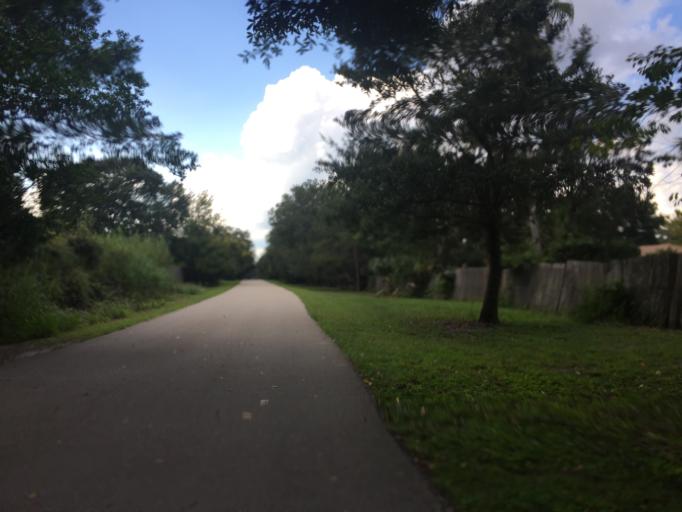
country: US
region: Florida
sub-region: Seminole County
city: Oviedo
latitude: 28.6769
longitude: -81.2140
